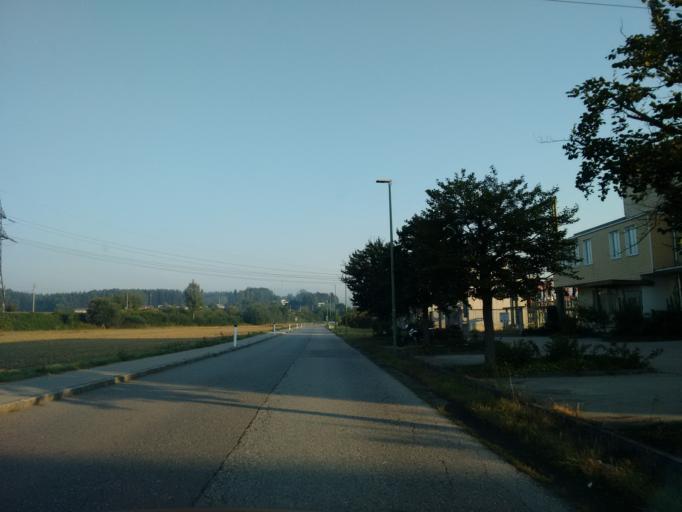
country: AT
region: Upper Austria
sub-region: Wels Stadt
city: Wels
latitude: 48.1832
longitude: 14.0053
